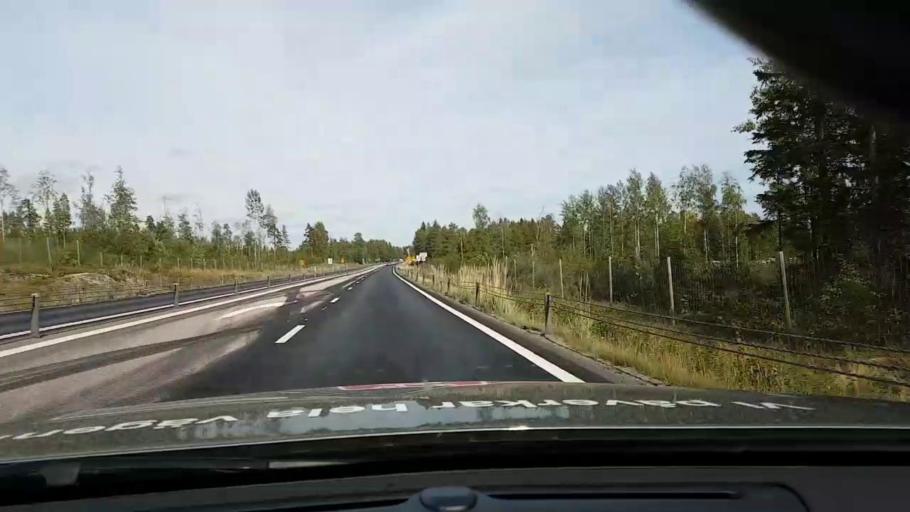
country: SE
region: Vaesternorrland
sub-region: OErnskoeldsviks Kommun
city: Husum
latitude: 63.4775
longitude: 19.2916
